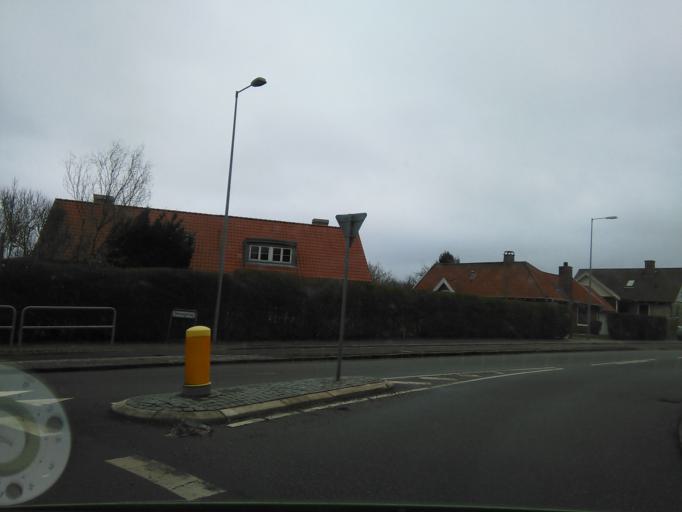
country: DK
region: Central Jutland
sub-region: Arhus Kommune
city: Arhus
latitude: 56.1917
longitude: 10.2286
